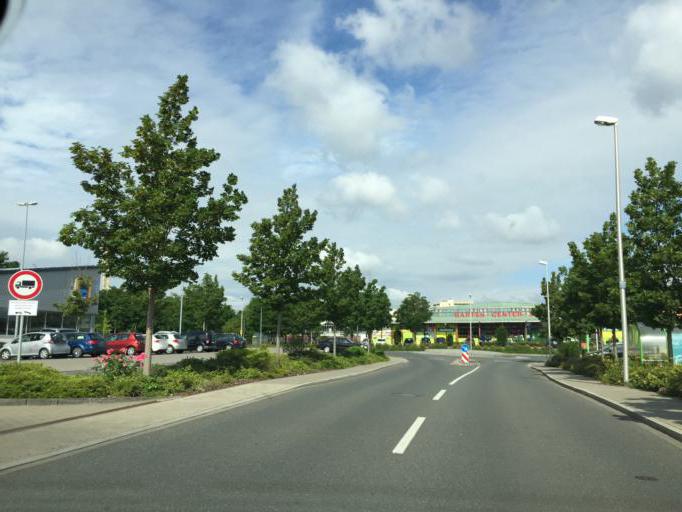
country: DE
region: Bavaria
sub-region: Regierungsbezirk Mittelfranken
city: Erlangen
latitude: 49.5756
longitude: 11.0015
